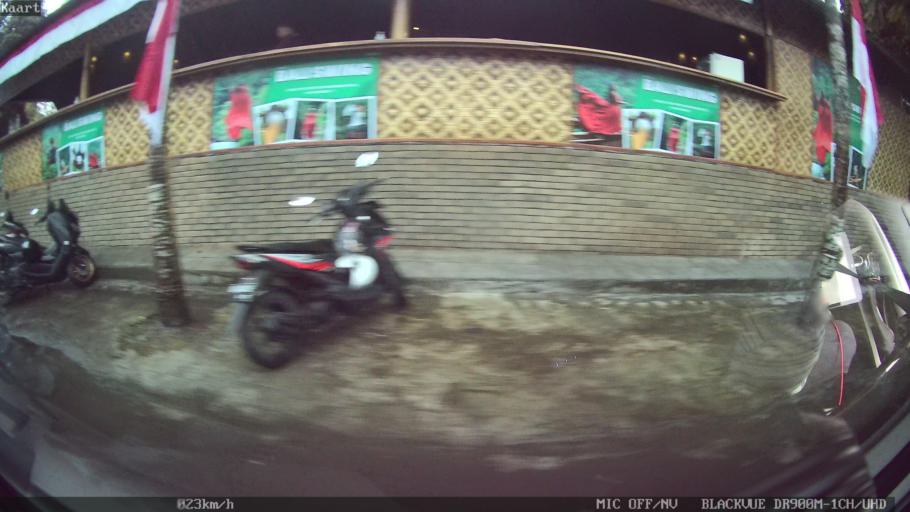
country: ID
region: Bali
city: Pegongan
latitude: -8.4902
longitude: 115.2399
